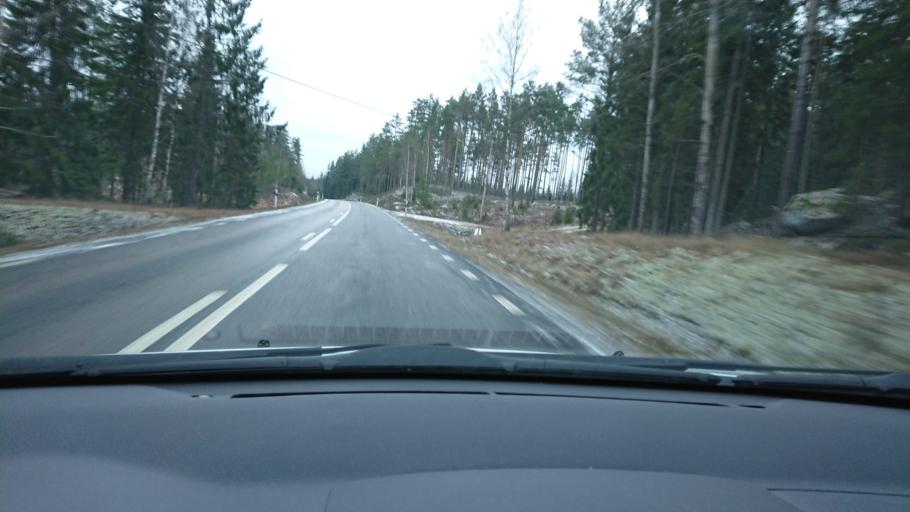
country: SE
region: Kalmar
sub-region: Hultsfreds Kommun
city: Virserum
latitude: 57.2390
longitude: 15.5419
